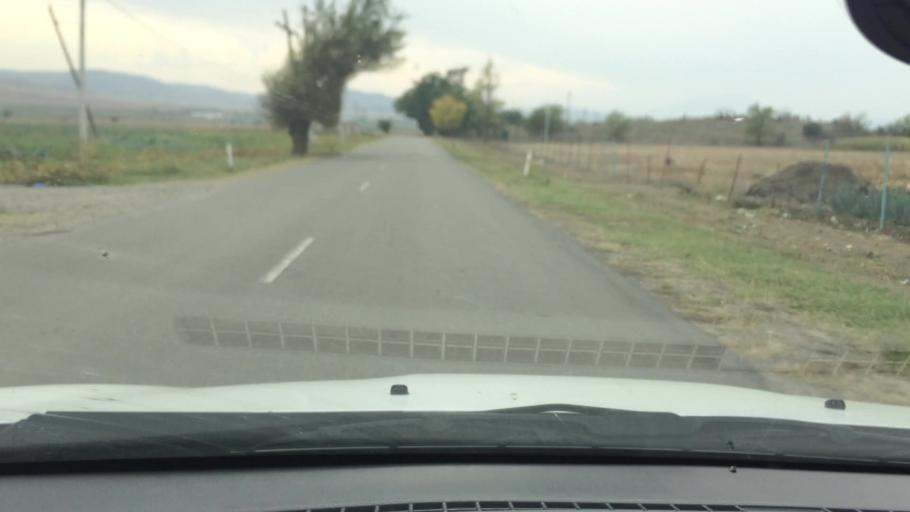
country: AM
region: Tavush
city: Berdavan
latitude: 41.3514
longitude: 44.9614
